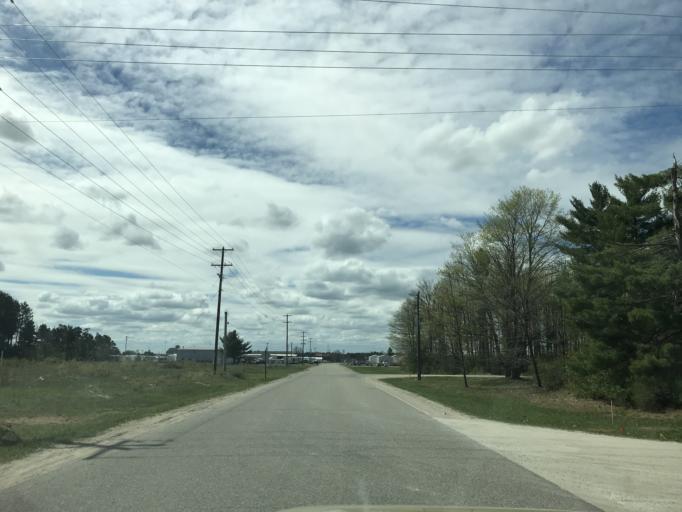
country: US
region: Michigan
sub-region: Otsego County
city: Gaylord
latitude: 45.0350
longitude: -84.6918
